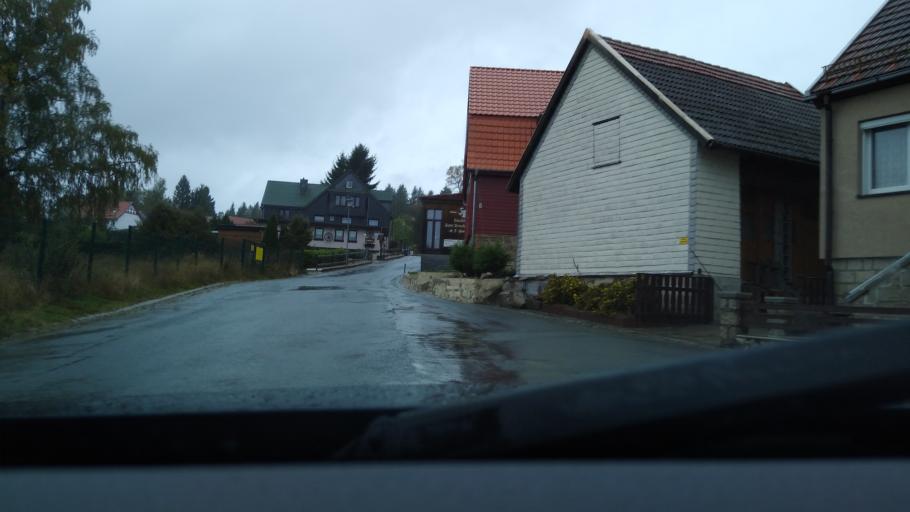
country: DE
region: Saxony-Anhalt
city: Benneckenstein
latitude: 51.6984
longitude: 10.7188
